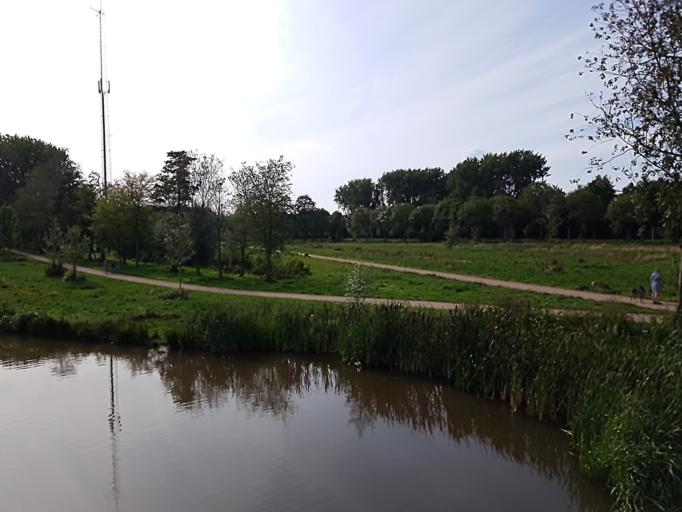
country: NL
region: North Brabant
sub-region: Gemeente Eindhoven
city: Eindhoven
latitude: 51.4340
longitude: 5.4614
